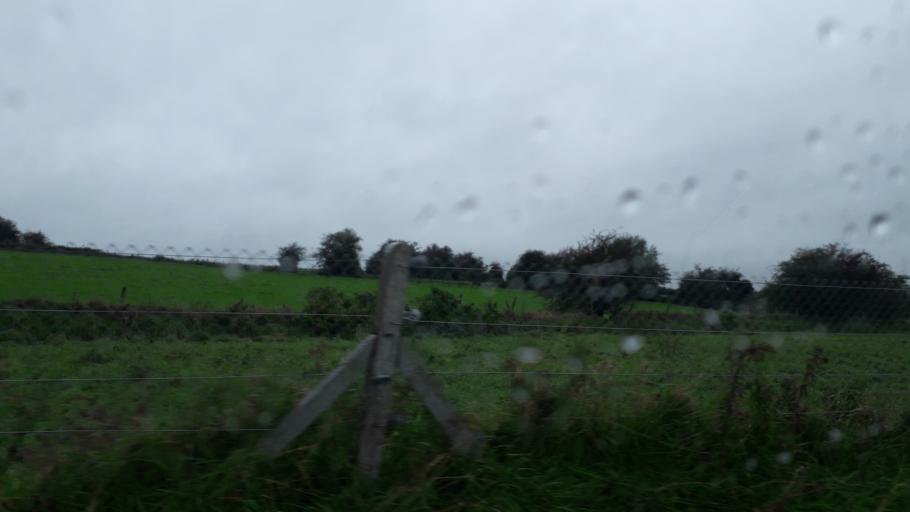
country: IE
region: Connaught
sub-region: Roscommon
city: Roscommon
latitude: 53.7822
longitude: -8.2606
